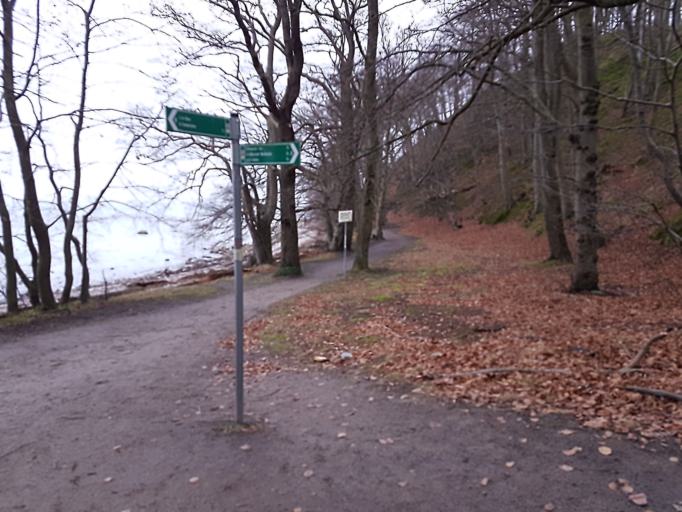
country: DE
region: Mecklenburg-Vorpommern
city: Ostseebad Binz
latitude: 54.3988
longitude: 13.6325
